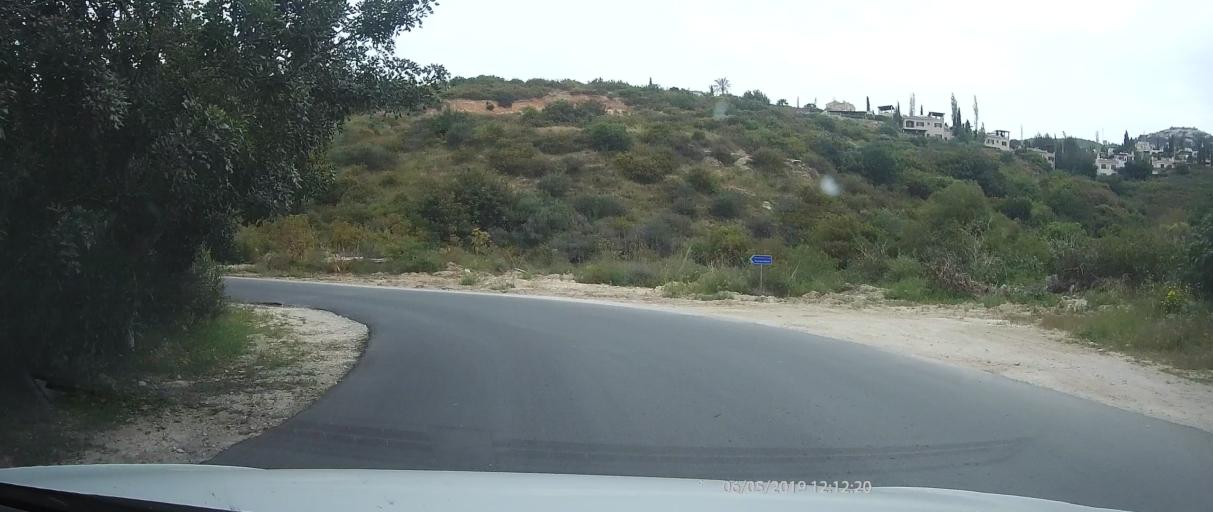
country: CY
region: Pafos
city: Tala
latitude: 34.8413
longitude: 32.4282
